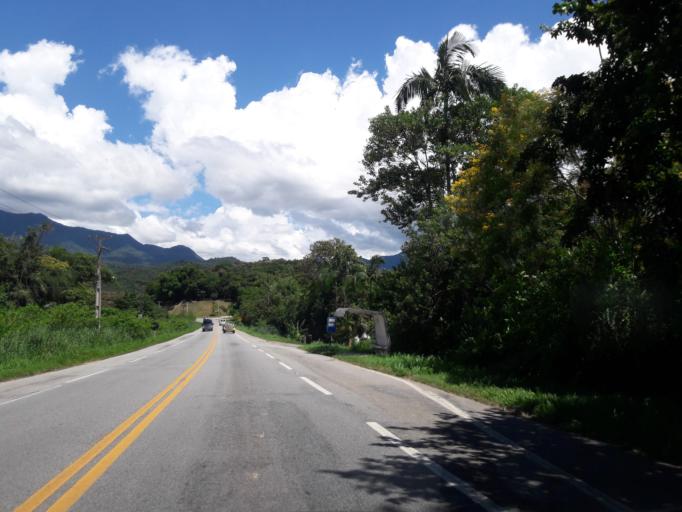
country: BR
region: Parana
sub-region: Antonina
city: Antonina
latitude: -25.5391
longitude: -48.7943
